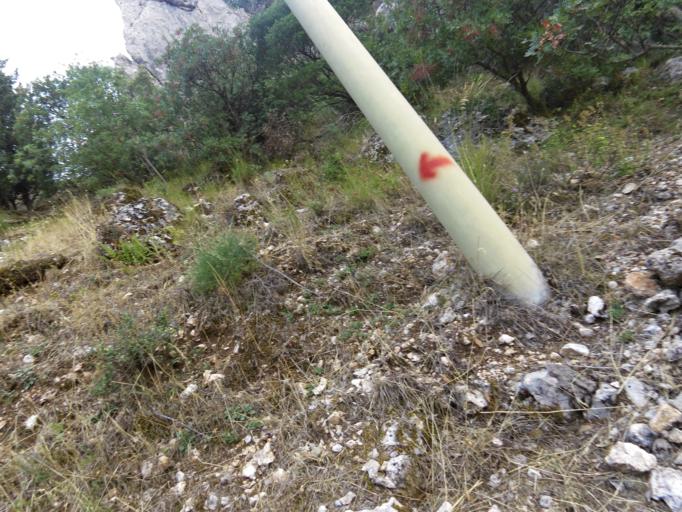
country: IT
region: Calabria
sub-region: Provincia di Reggio Calabria
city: Pazzano
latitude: 38.4714
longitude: 16.4500
